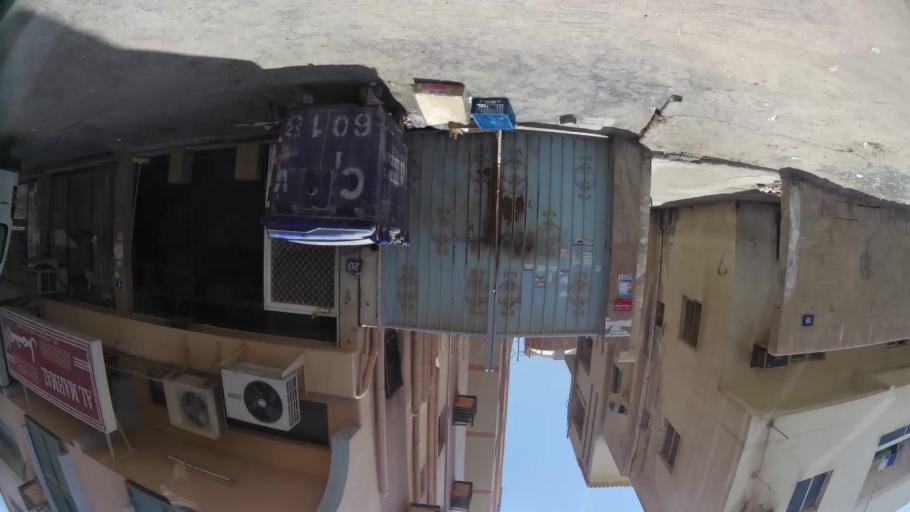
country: AE
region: Ajman
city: Ajman
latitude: 25.4091
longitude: 55.4420
